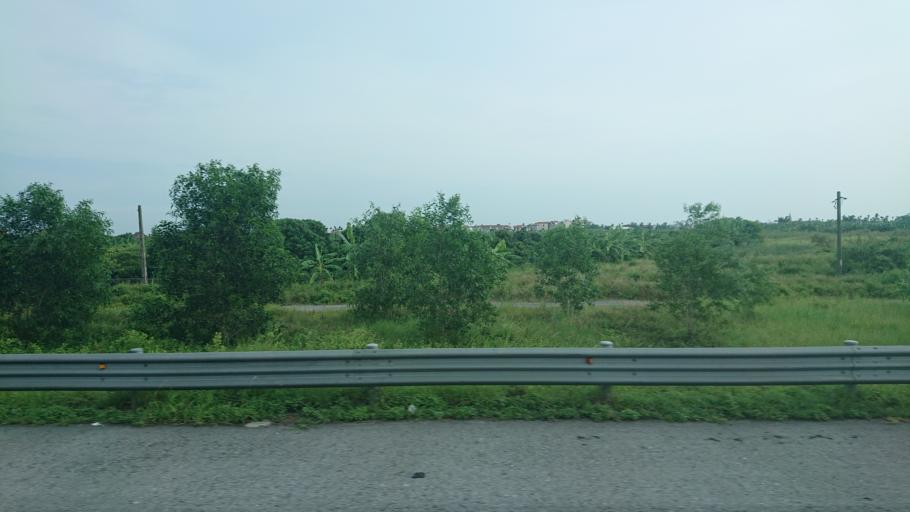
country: VN
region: Hai Phong
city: An Lao
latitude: 20.8150
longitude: 106.4937
